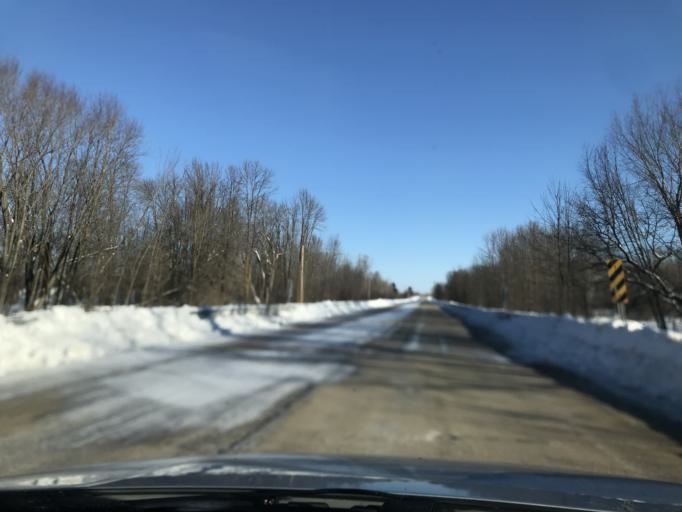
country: US
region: Wisconsin
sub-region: Oconto County
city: Oconto Falls
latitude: 44.9723
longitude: -88.0459
